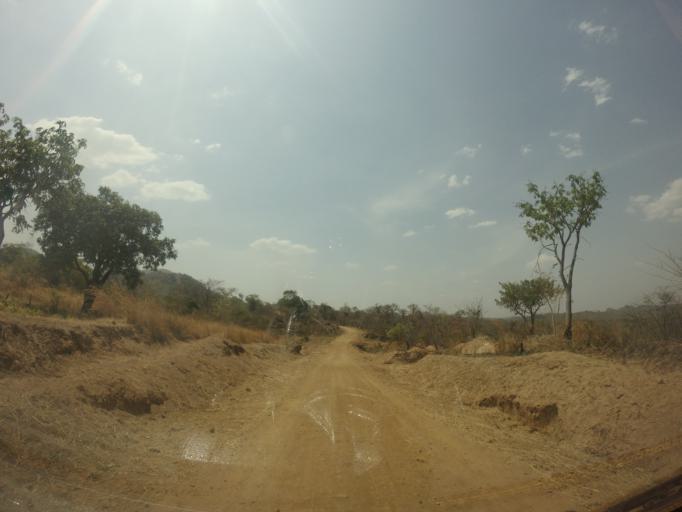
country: UG
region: Northern Region
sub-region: Arua District
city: Arua
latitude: 2.8973
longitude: 31.1128
